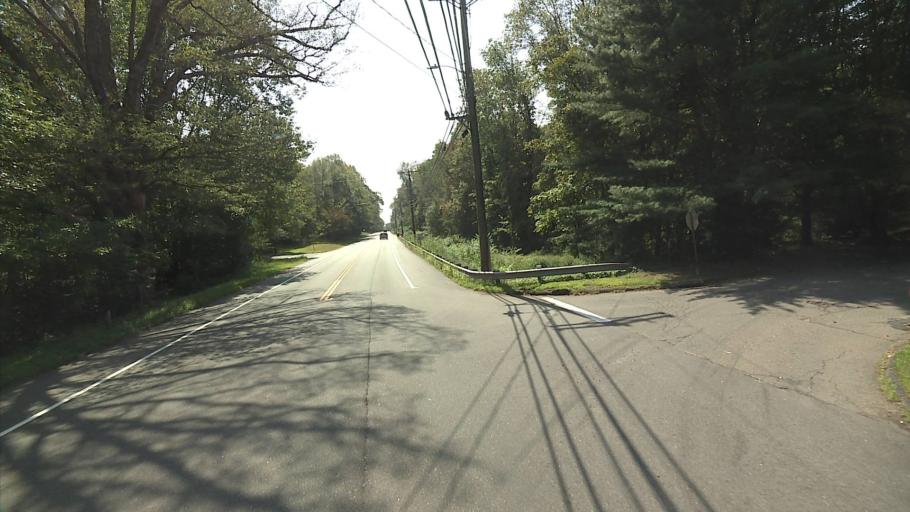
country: US
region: Connecticut
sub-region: New Haven County
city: Madison Center
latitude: 41.3480
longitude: -72.6318
